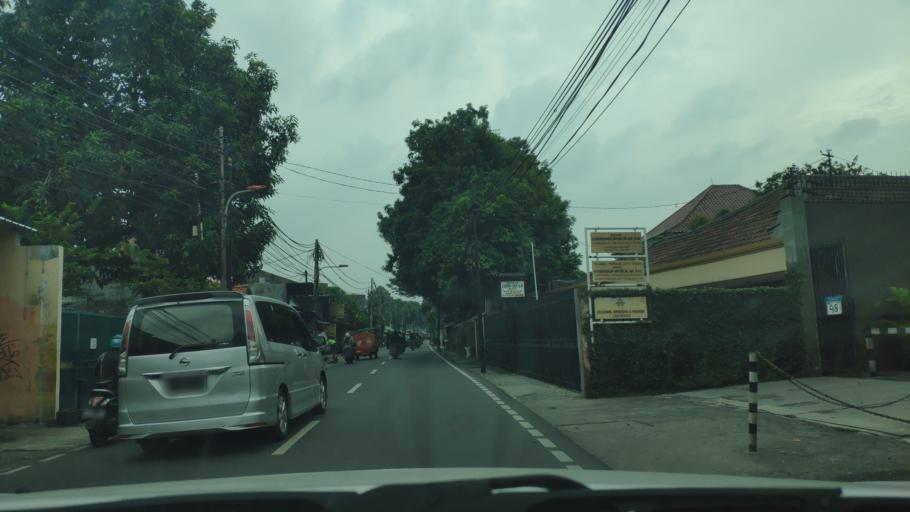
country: ID
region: Jakarta Raya
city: Jakarta
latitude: -6.1901
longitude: 106.7861
